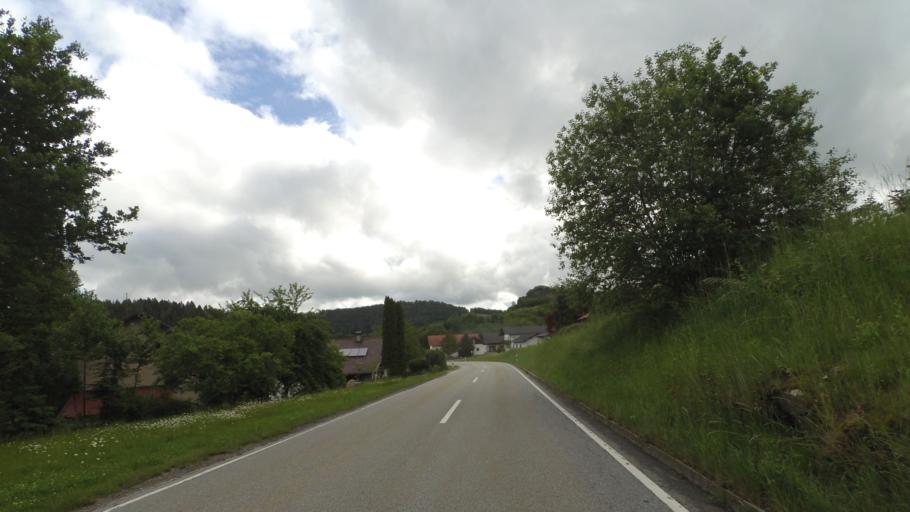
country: DE
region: Bavaria
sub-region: Lower Bavaria
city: Rattenberg
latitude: 49.0951
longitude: 12.7457
